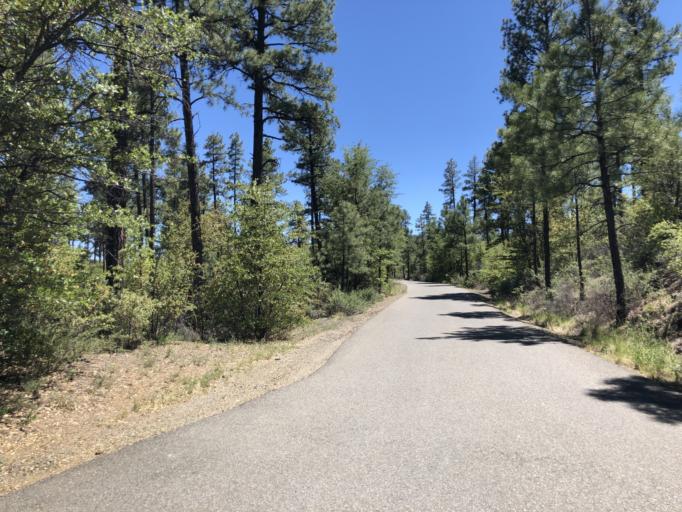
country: US
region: Arizona
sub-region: Yavapai County
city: Prescott
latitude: 34.5172
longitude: -112.3908
